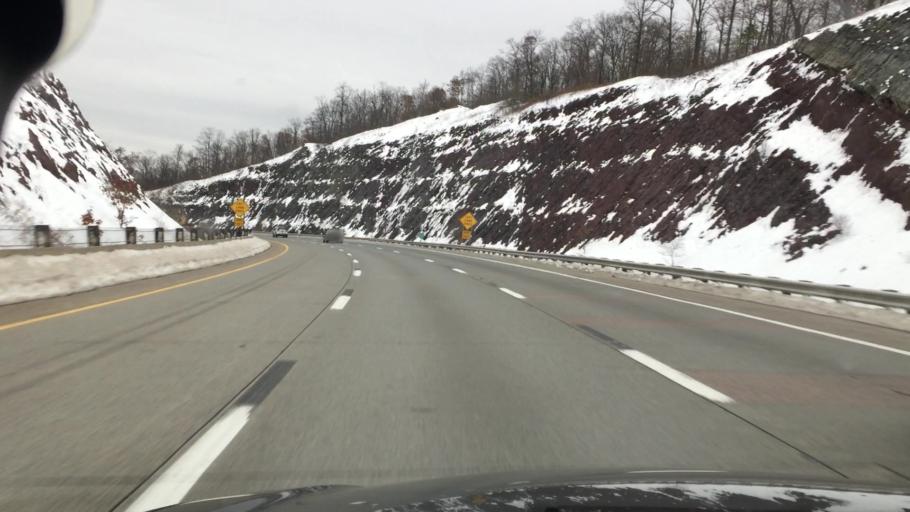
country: US
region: Pennsylvania
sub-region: Luzerne County
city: Nanticoke
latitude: 41.1731
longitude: -75.9561
